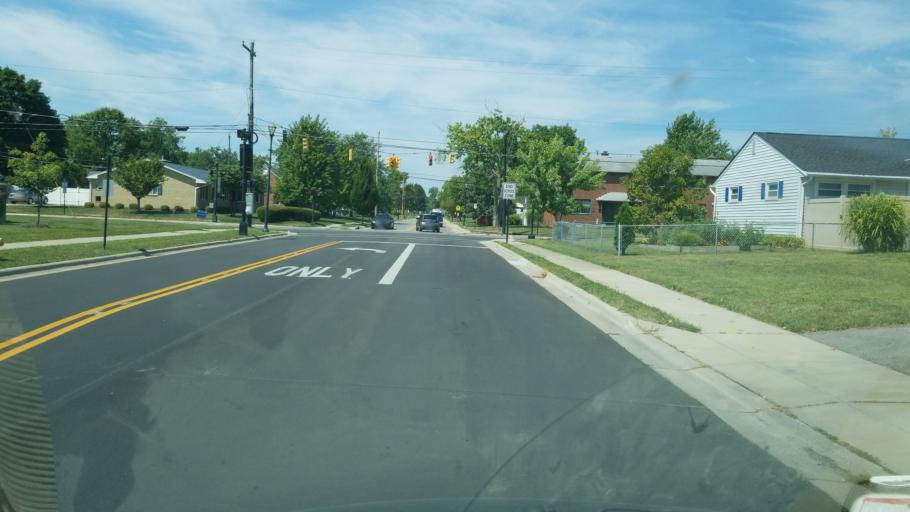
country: US
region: Ohio
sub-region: Franklin County
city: Grove City
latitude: 39.8777
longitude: -83.0850
